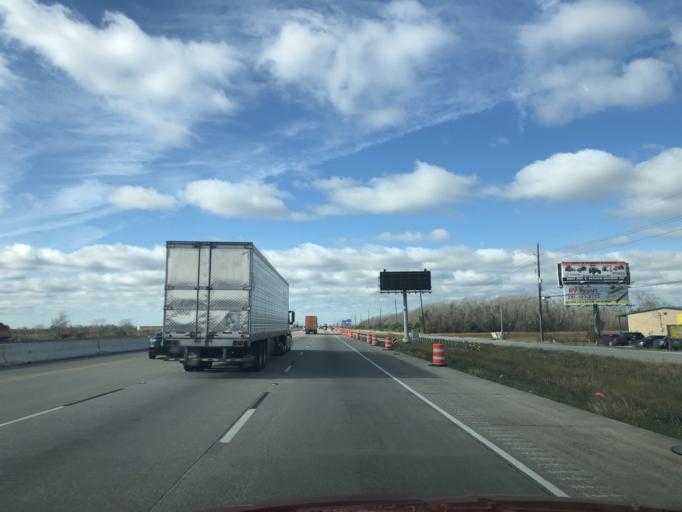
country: US
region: Texas
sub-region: Chambers County
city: Old River-Winfree
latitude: 29.8278
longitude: -94.8293
